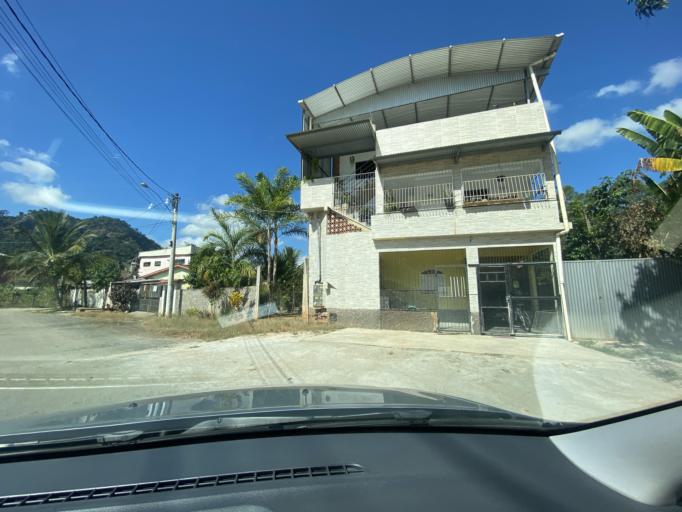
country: BR
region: Espirito Santo
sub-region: Jeronimo Monteiro
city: Jeronimo Monteiro
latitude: -20.7968
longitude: -41.4060
